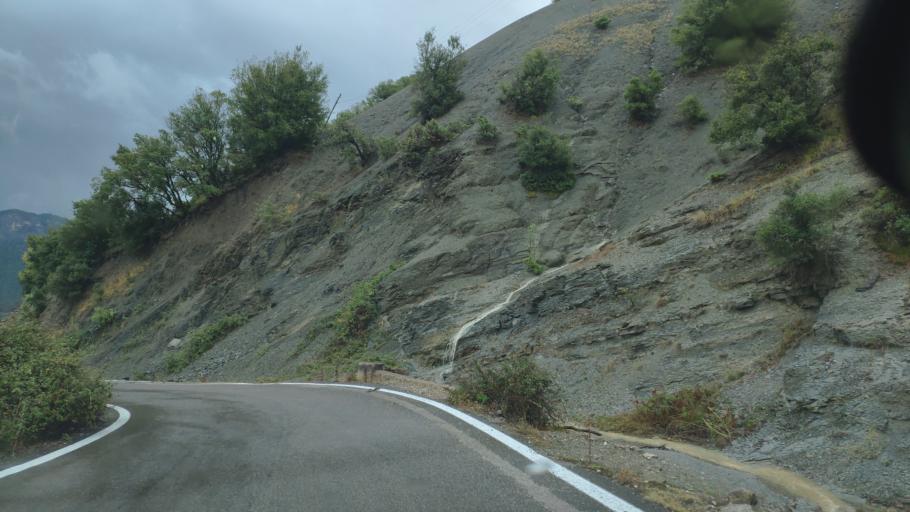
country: GR
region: Thessaly
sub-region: Nomos Kardhitsas
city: Anthiro
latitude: 39.1074
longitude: 21.4136
